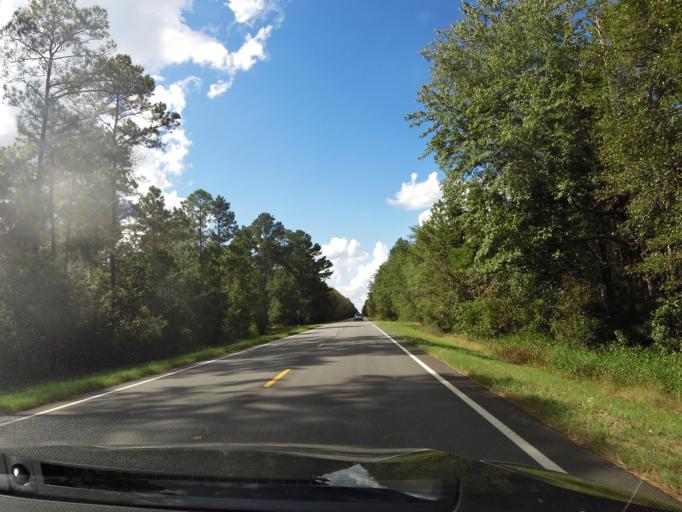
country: US
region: Georgia
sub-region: Echols County
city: Statenville
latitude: 30.7279
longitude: -83.0810
